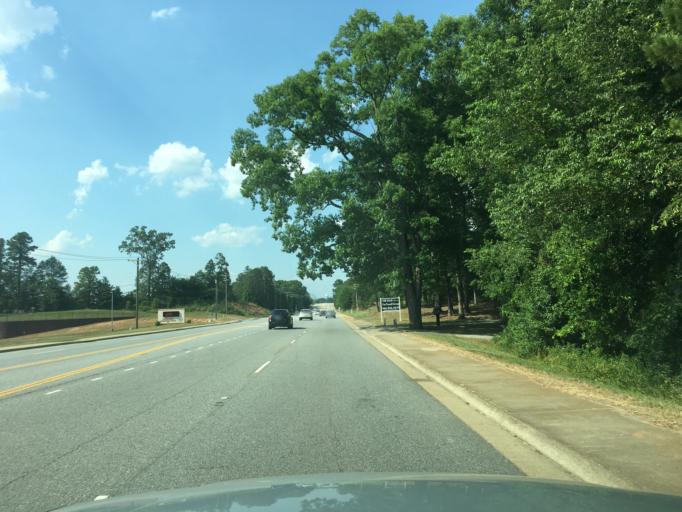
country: US
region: South Carolina
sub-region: Anderson County
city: Northlake
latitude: 34.5809
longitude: -82.6217
